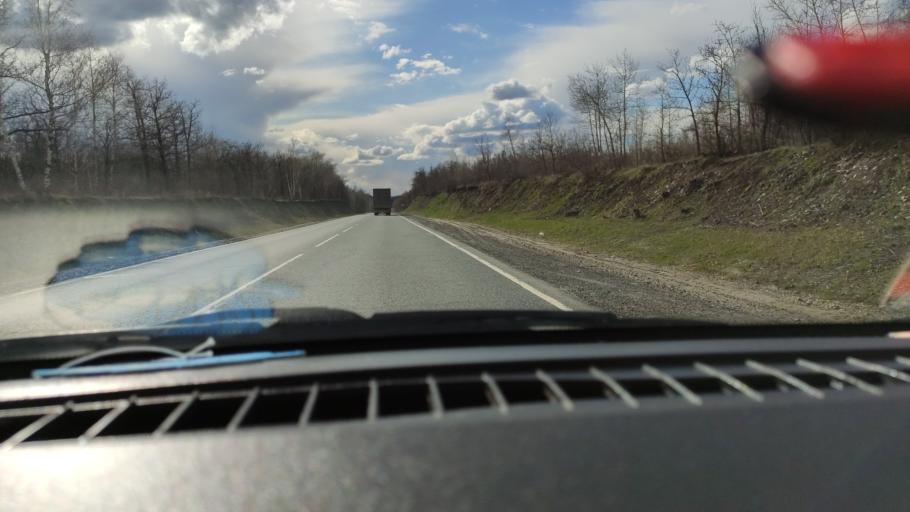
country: RU
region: Saratov
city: Vol'sk
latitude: 52.1107
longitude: 47.3487
